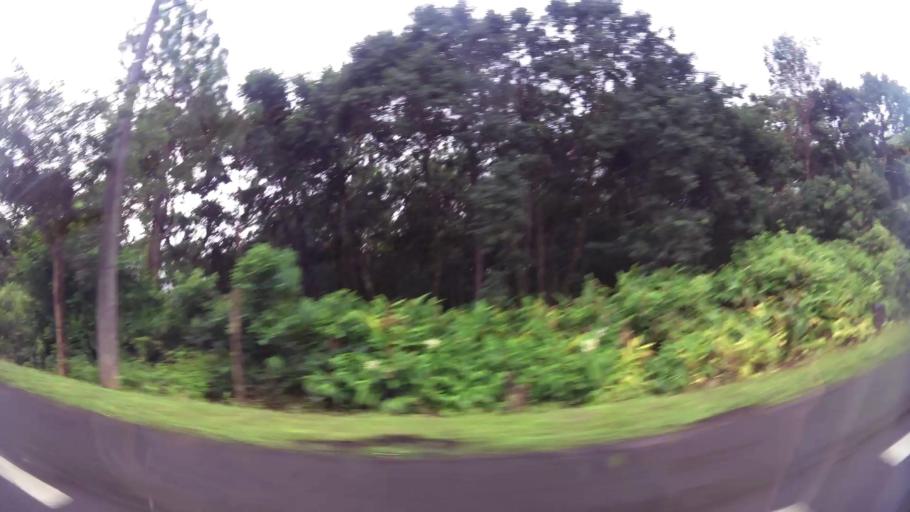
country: MU
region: Plaines Wilhems
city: Curepipe
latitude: -20.3114
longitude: 57.5423
